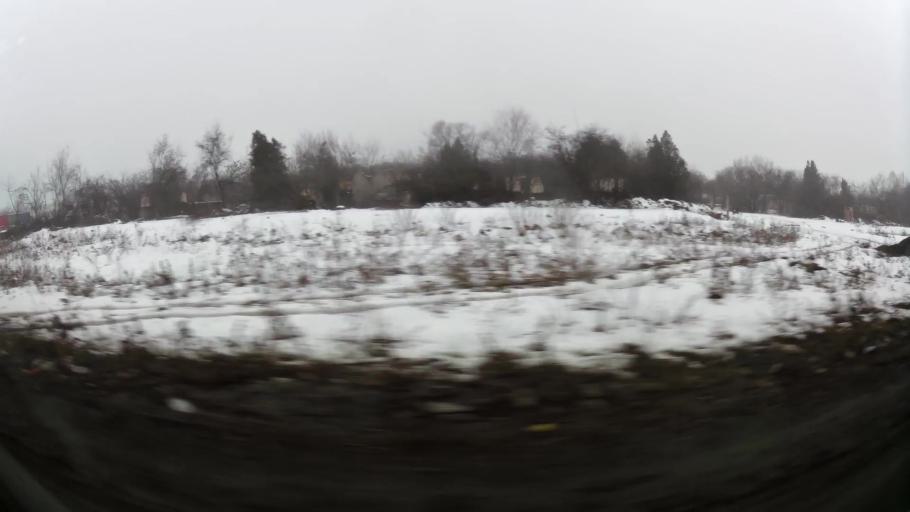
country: RO
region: Ilfov
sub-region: Comuna Clinceni
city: Olteni
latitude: 44.4034
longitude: 25.9778
